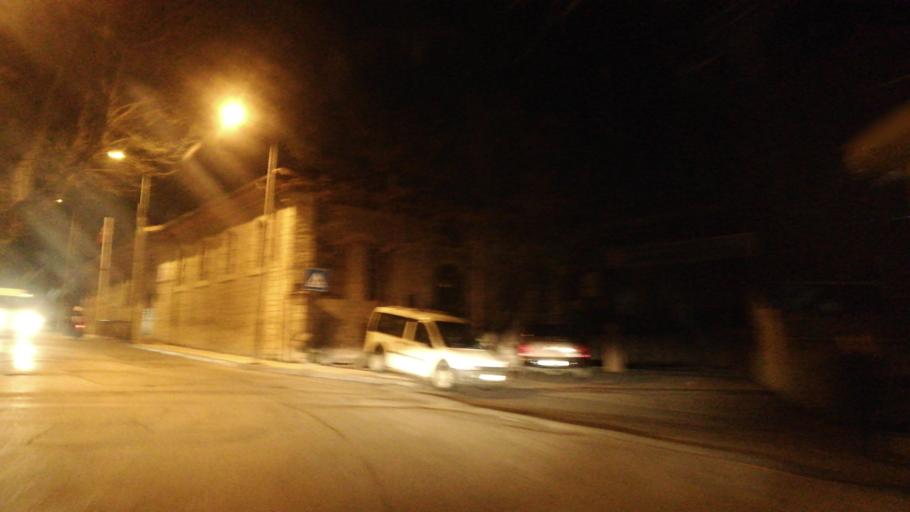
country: TR
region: Kahramanmaras
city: Kahramanmaras
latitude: 37.5850
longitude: 36.9293
